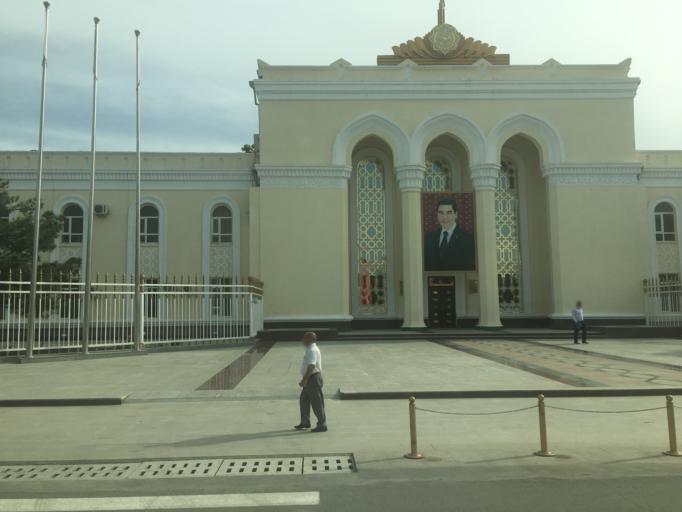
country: TM
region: Mary
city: Mary
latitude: 37.5934
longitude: 61.8397
